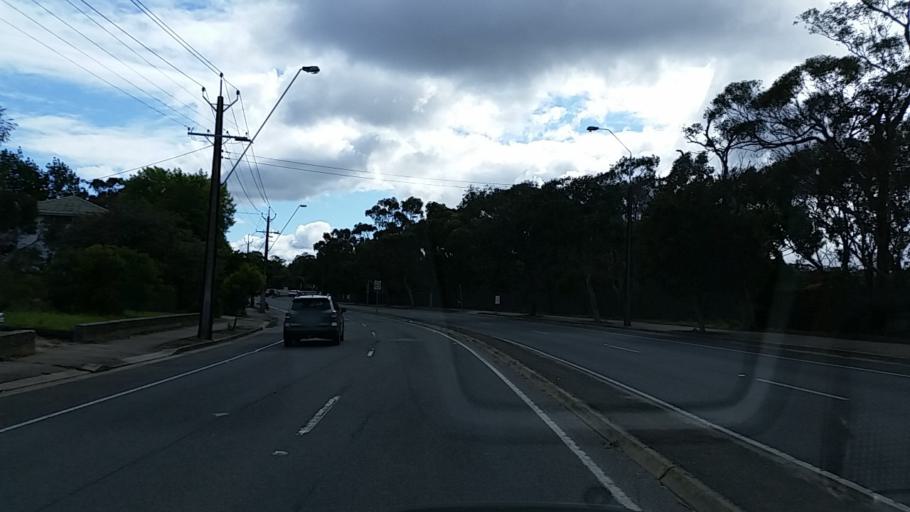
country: AU
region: South Australia
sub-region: Mitcham
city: Blackwood
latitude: -35.0233
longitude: 138.6074
